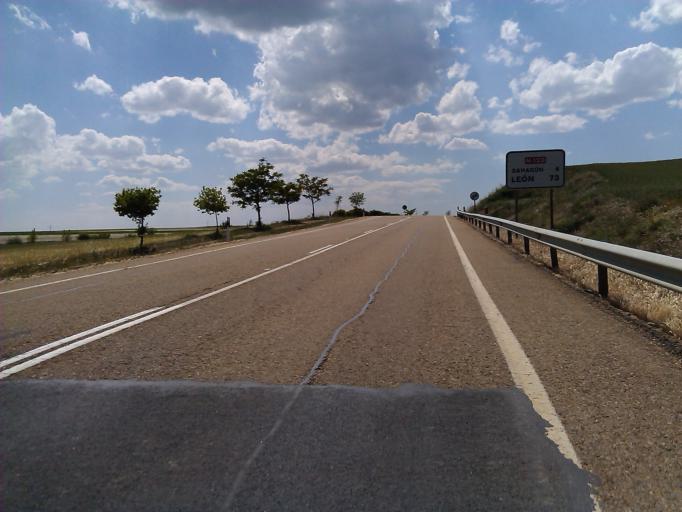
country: ES
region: Castille and Leon
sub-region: Provincia de Palencia
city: Moratinos
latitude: 42.3652
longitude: -4.9580
